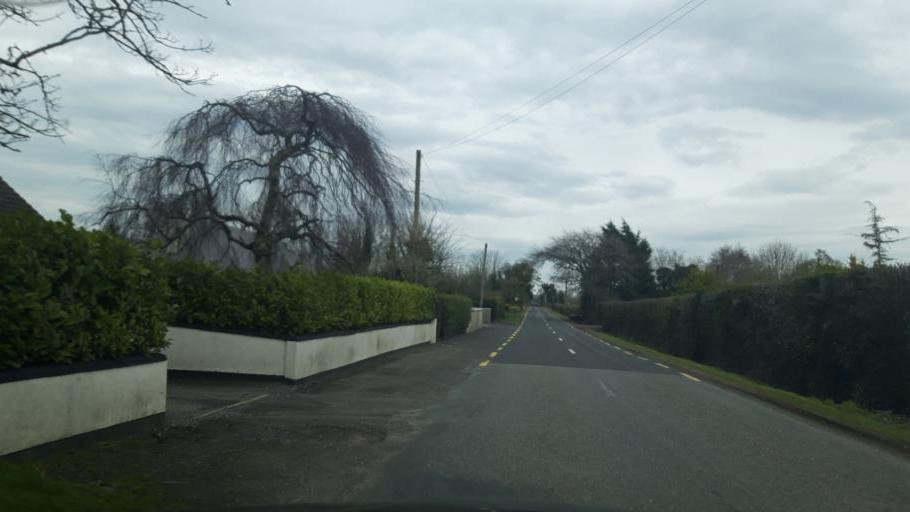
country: IE
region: Leinster
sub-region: Kildare
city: Clane
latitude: 53.3300
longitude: -6.6863
